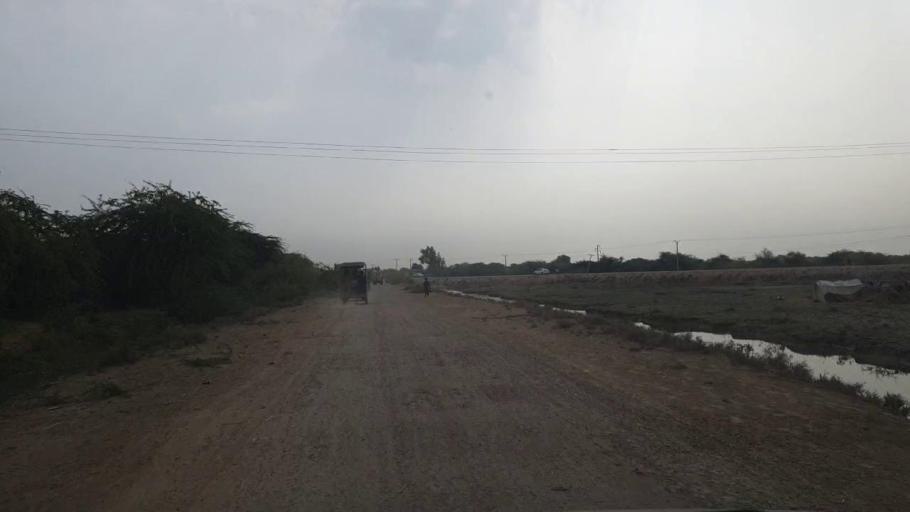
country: PK
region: Sindh
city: Talhar
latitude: 24.8990
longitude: 68.7740
